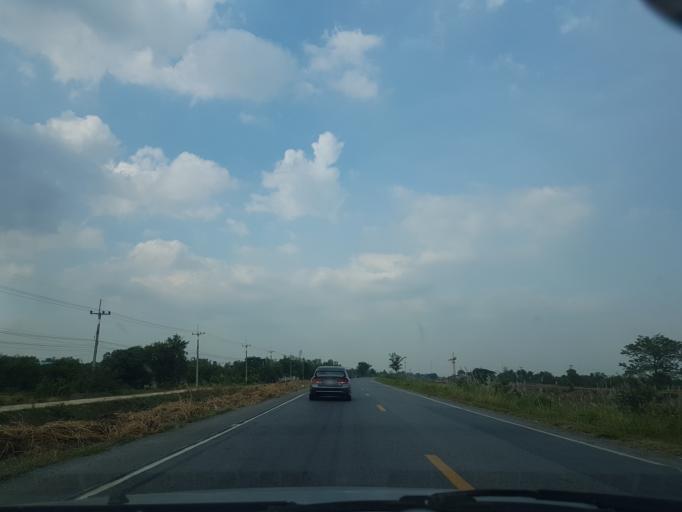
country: TH
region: Phra Nakhon Si Ayutthaya
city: Phachi
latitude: 14.4925
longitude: 100.7362
